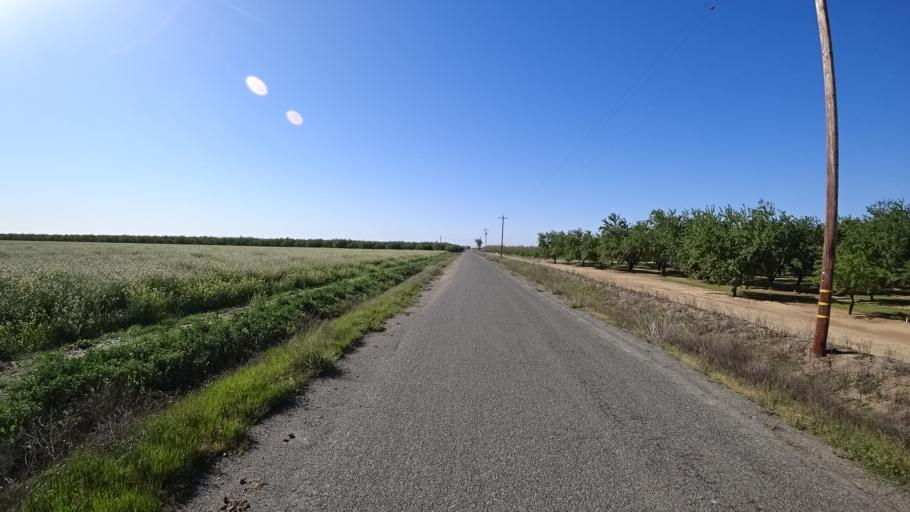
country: US
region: California
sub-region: Glenn County
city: Hamilton City
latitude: 39.6998
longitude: -122.0742
